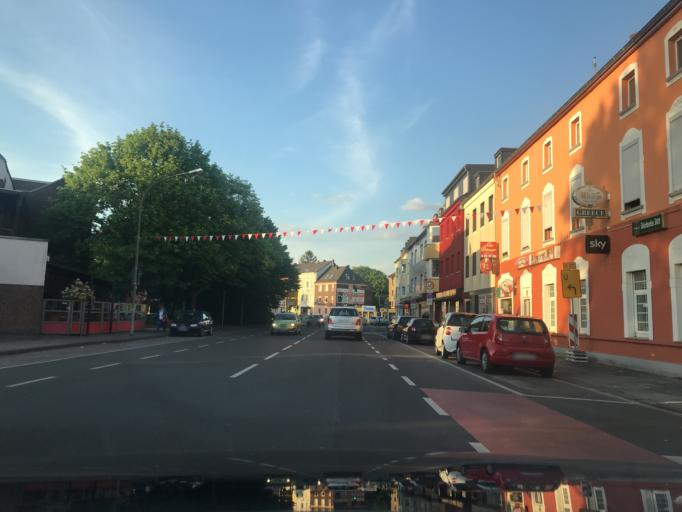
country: DE
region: North Rhine-Westphalia
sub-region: Regierungsbezirk Dusseldorf
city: Monchengladbach
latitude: 51.1918
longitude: 6.4238
